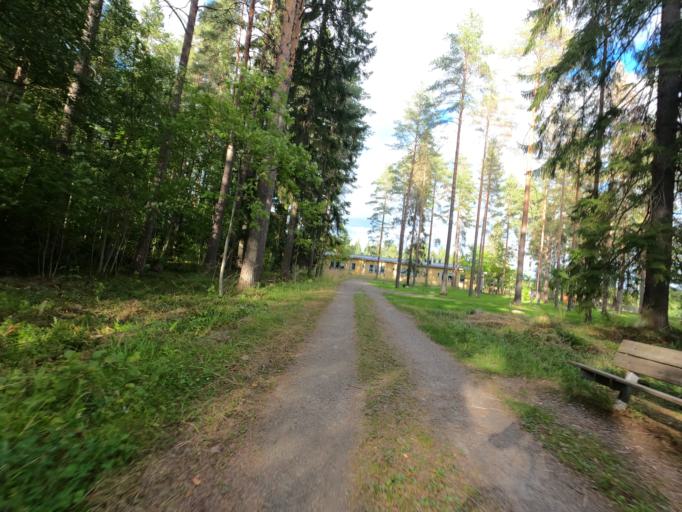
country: FI
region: North Karelia
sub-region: Joensuu
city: Joensuu
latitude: 62.6031
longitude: 29.7219
